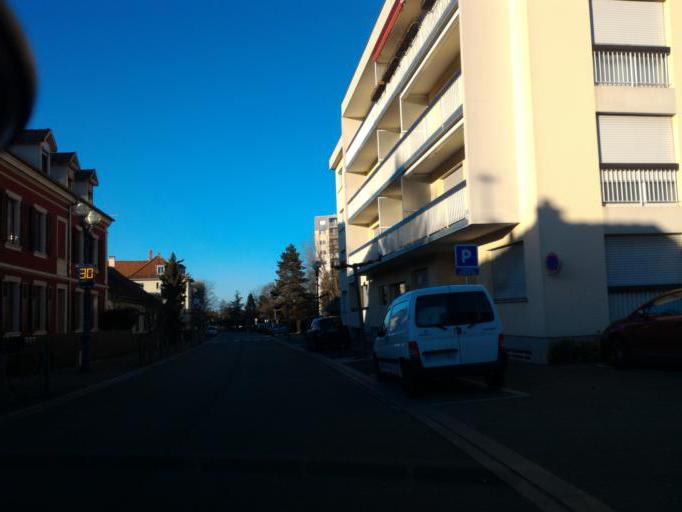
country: FR
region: Alsace
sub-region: Departement du Haut-Rhin
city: Riedisheim
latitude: 47.7522
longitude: 7.3691
